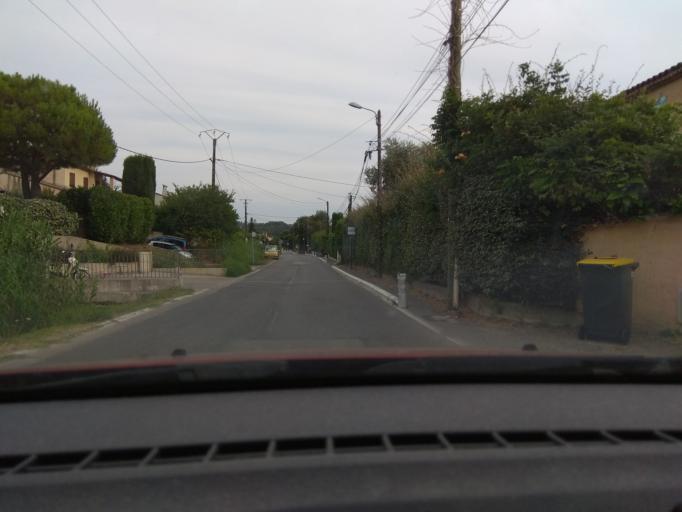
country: FR
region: Provence-Alpes-Cote d'Azur
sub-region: Departement des Alpes-Maritimes
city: La Colle-sur-Loup
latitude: 43.6782
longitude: 7.1076
